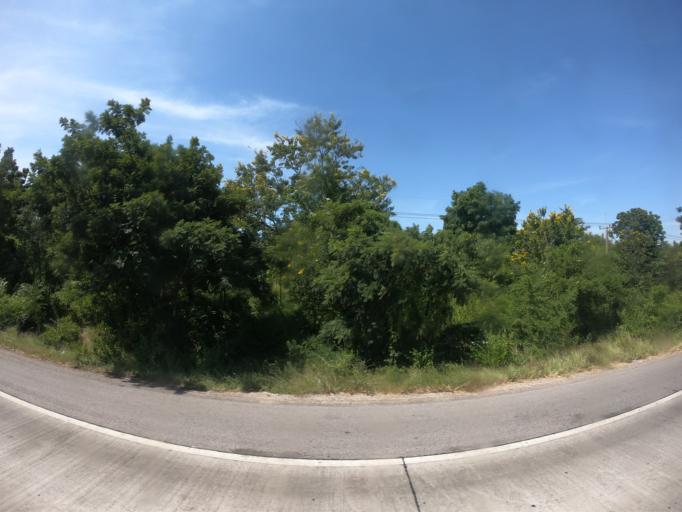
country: TH
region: Nakhon Ratchasima
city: Sida
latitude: 15.5628
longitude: 102.5517
